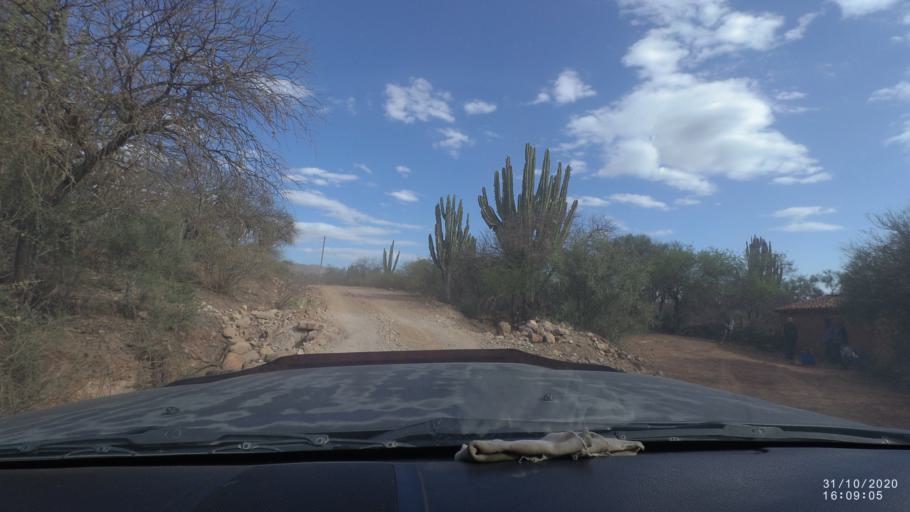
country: BO
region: Chuquisaca
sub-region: Provincia Zudanez
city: Mojocoya
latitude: -18.3867
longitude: -64.6383
